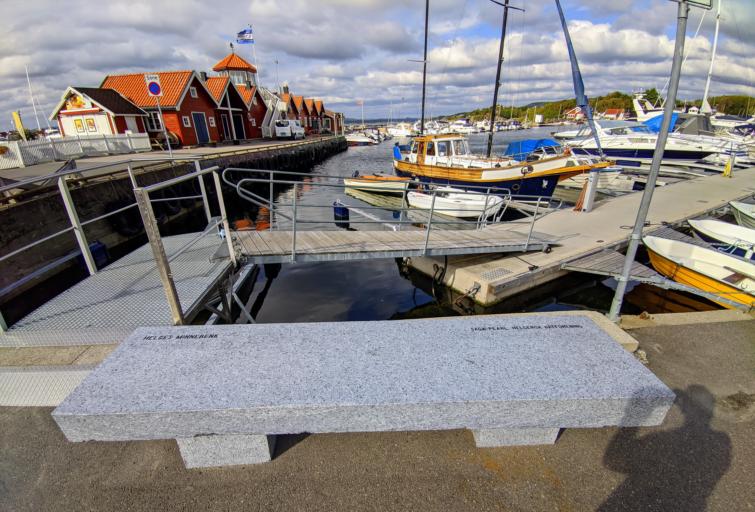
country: NO
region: Telemark
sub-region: Bamble
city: Langesund
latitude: 58.9939
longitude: 9.8581
